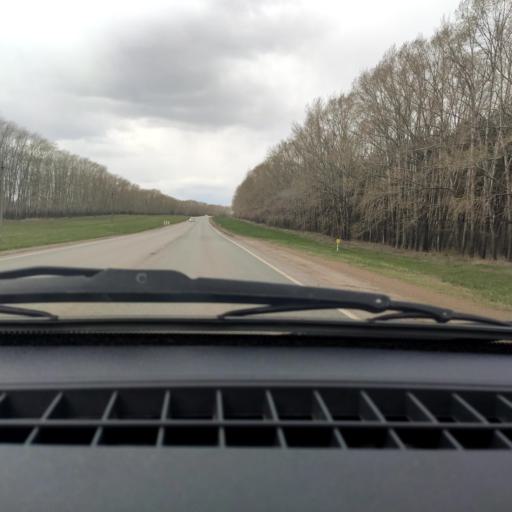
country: RU
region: Bashkortostan
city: Kushnarenkovo
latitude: 55.0871
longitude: 55.3526
